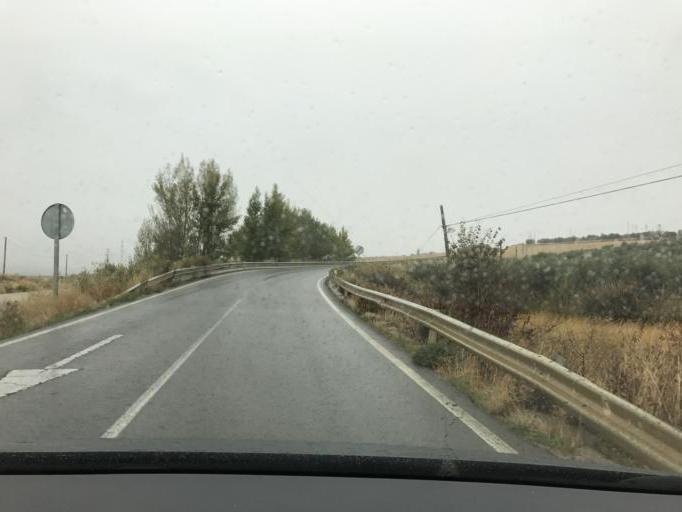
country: ES
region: Andalusia
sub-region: Provincia de Granada
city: Escuzar
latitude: 37.0912
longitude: -3.7372
